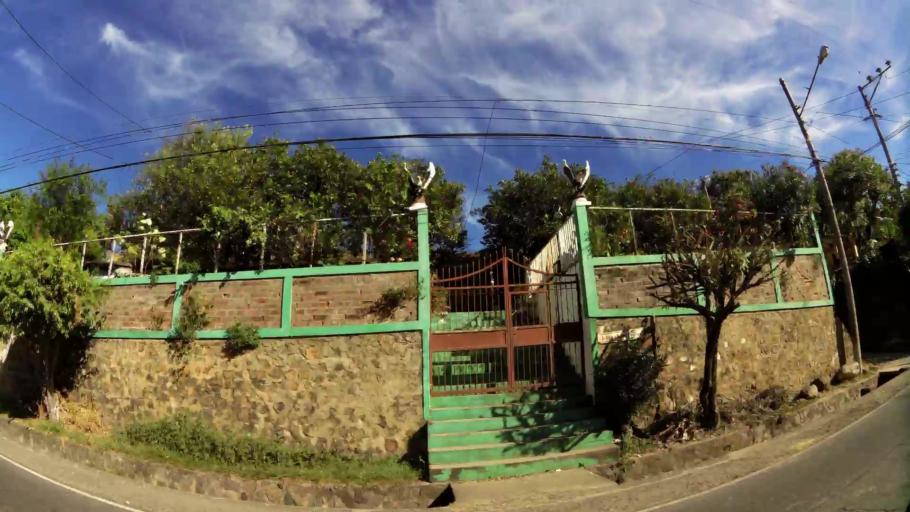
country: SV
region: Cuscatlan
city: Suchitoto
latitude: 13.9268
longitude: -89.0314
